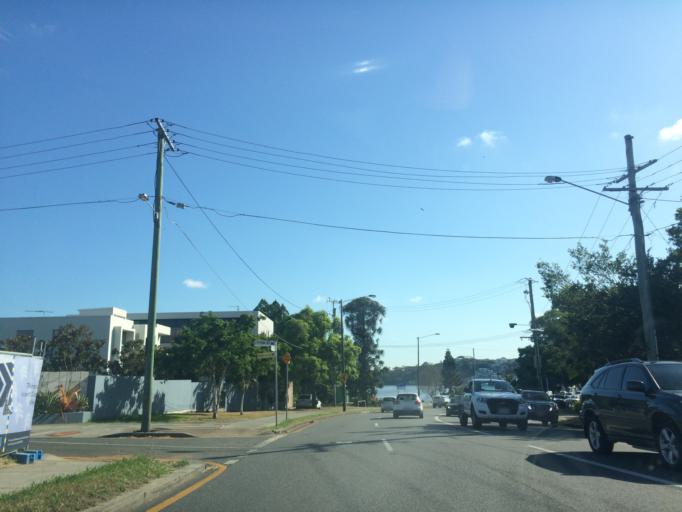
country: AU
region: Queensland
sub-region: Brisbane
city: Woolloongabba
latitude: -27.4772
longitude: 153.0488
